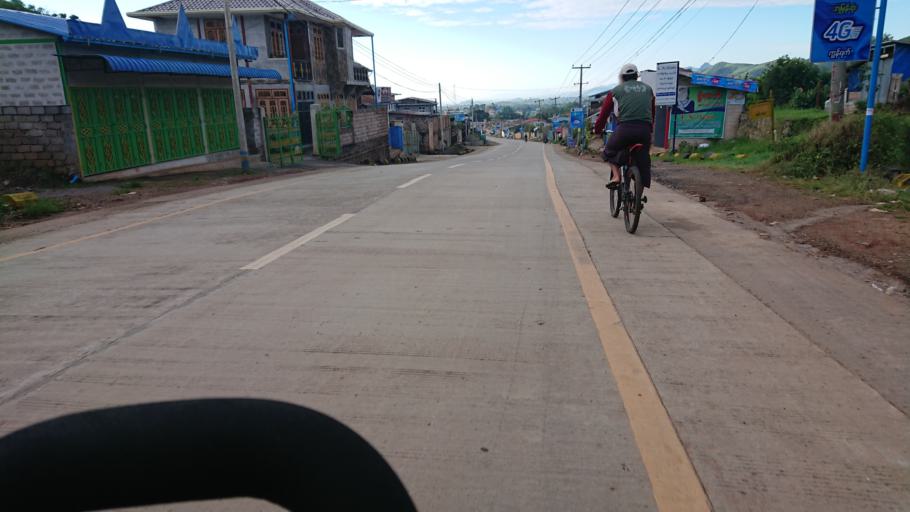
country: MM
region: Shan
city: Taunggyi
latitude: 20.7441
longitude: 97.0507
